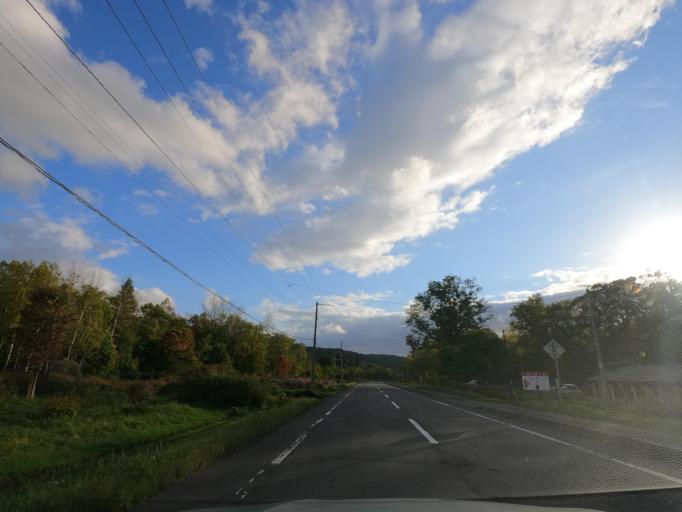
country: JP
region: Hokkaido
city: Date
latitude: 42.6447
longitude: 141.0525
